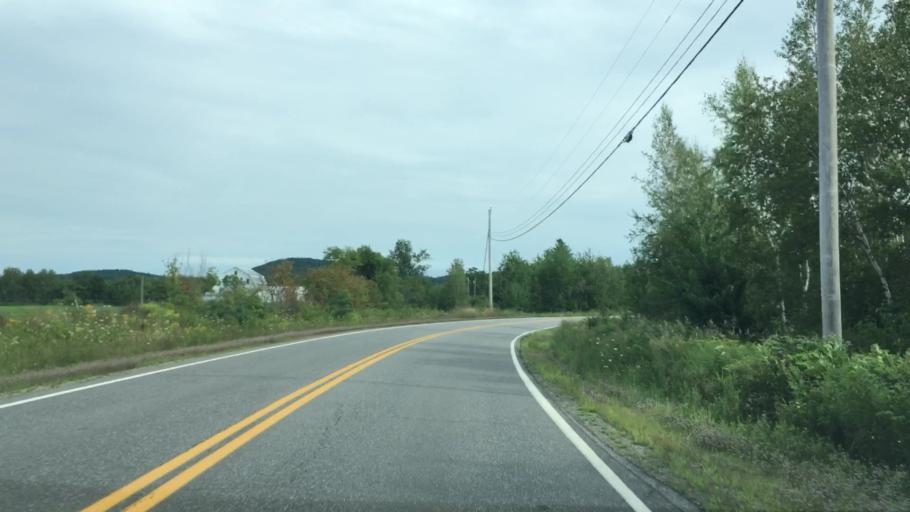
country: US
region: Maine
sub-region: Waldo County
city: Belfast
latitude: 44.3764
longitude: -69.0321
